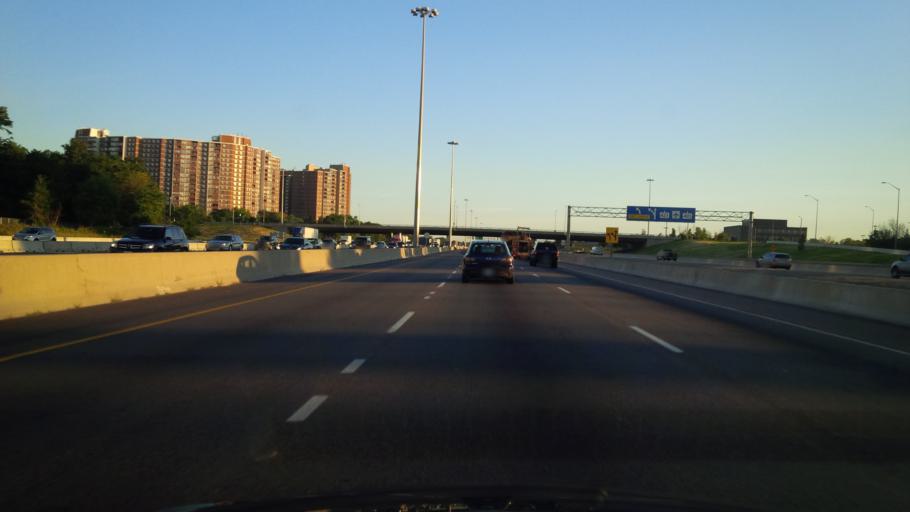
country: CA
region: Ontario
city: Etobicoke
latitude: 43.6518
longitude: -79.5662
